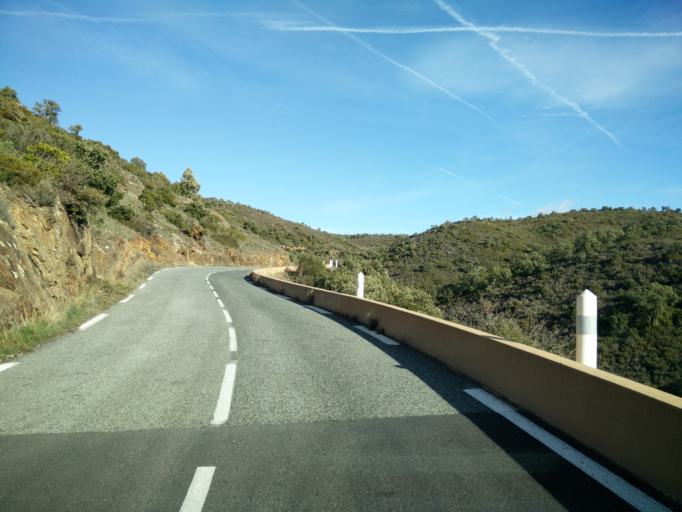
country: FR
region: Provence-Alpes-Cote d'Azur
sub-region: Departement du Var
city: Saint-Raphael
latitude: 43.4954
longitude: 6.7802
